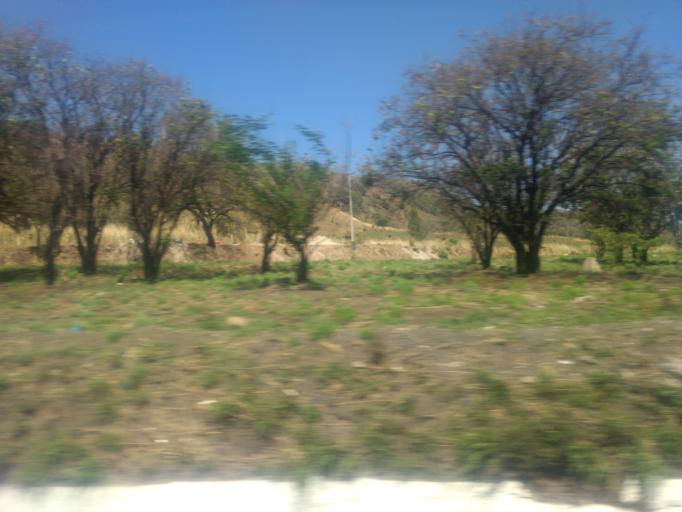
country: MX
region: Jalisco
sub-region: Acatlan de Juarez
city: Villa de los Ninos
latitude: 20.4245
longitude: -103.5530
